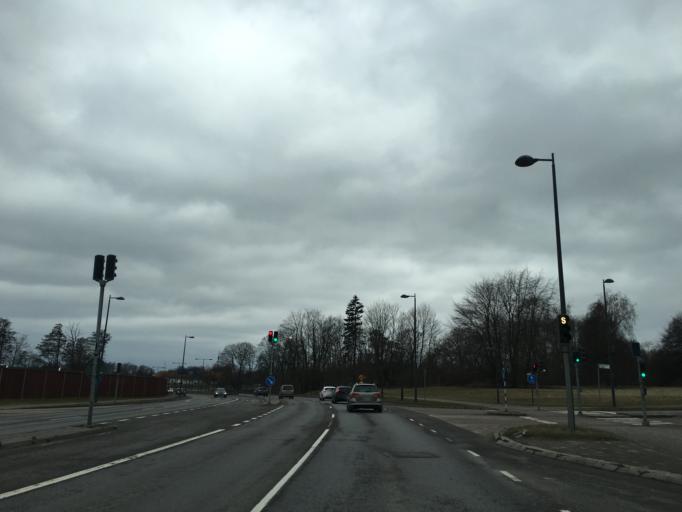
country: SE
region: Halland
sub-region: Halmstads Kommun
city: Halmstad
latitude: 56.6679
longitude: 12.8270
